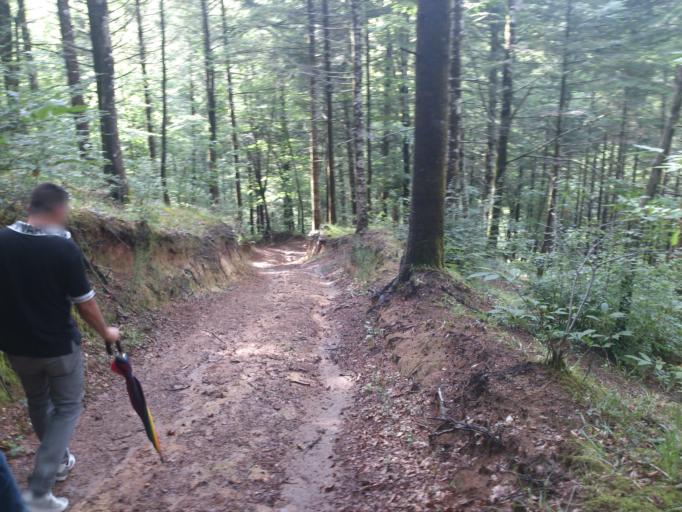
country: IT
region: Calabria
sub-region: Provincia di Vibo-Valentia
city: Serra San Bruno
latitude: 38.5478
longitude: 16.3101
